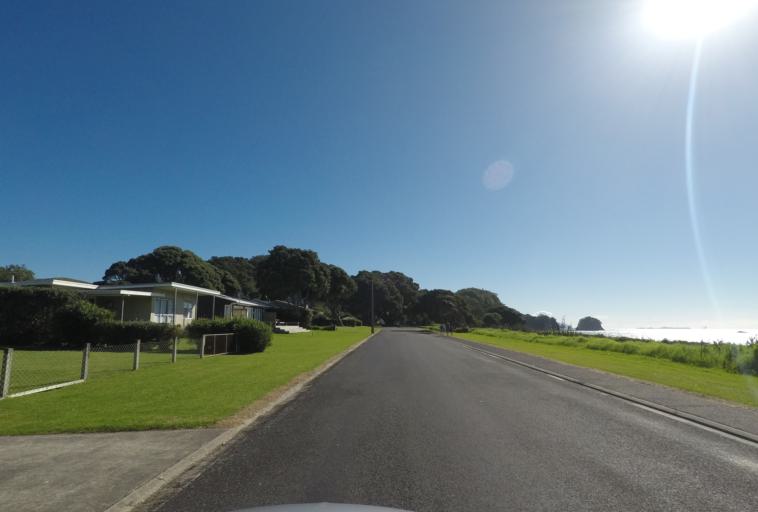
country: NZ
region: Waikato
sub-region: Thames-Coromandel District
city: Whangamata
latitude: -37.2809
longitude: 175.9012
